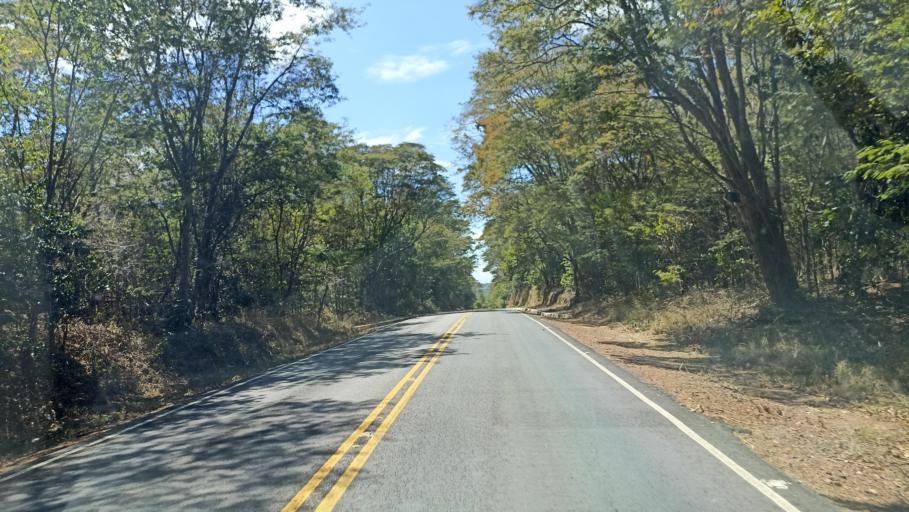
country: BR
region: Bahia
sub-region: Andarai
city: Vera Cruz
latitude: -12.7674
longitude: -41.3285
